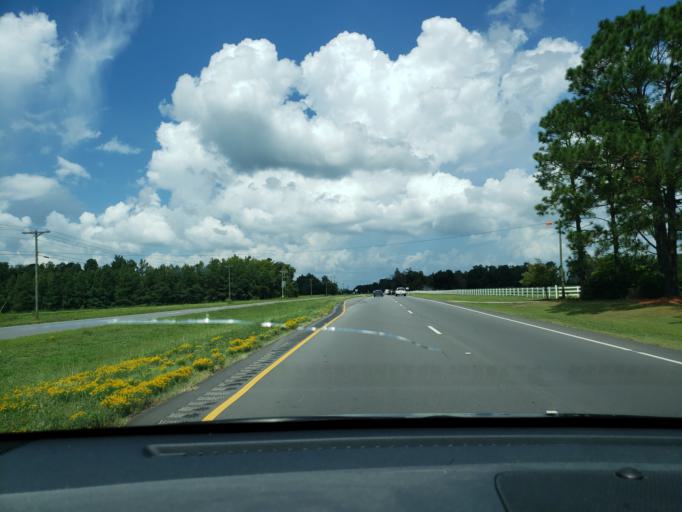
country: US
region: North Carolina
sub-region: Robeson County
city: Saint Pauls
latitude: 34.7690
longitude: -78.8104
